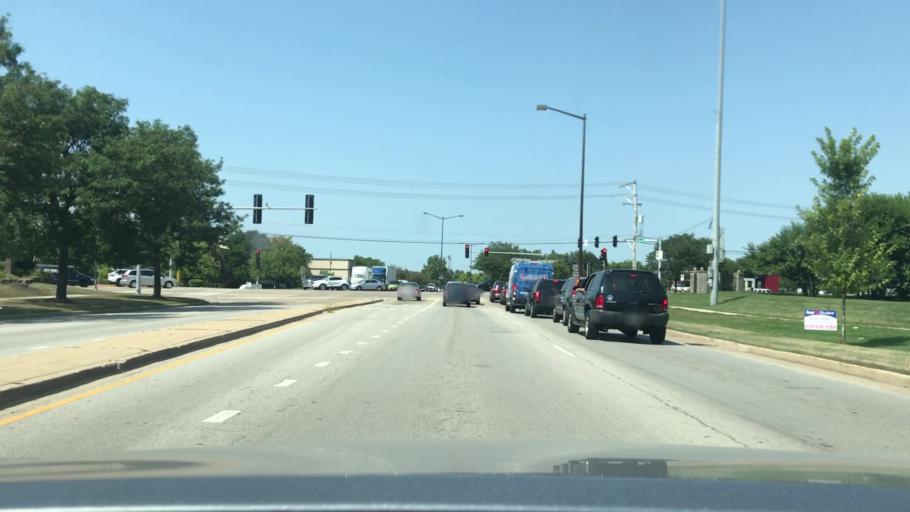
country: US
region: Illinois
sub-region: Kane County
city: Aurora
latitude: 41.7378
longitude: -88.2511
